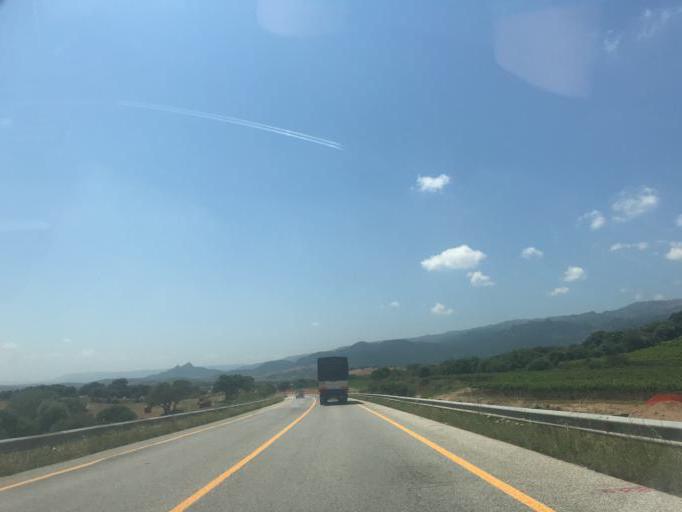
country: IT
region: Sardinia
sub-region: Provincia di Olbia-Tempio
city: Berchidda
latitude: 40.7811
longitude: 9.2217
